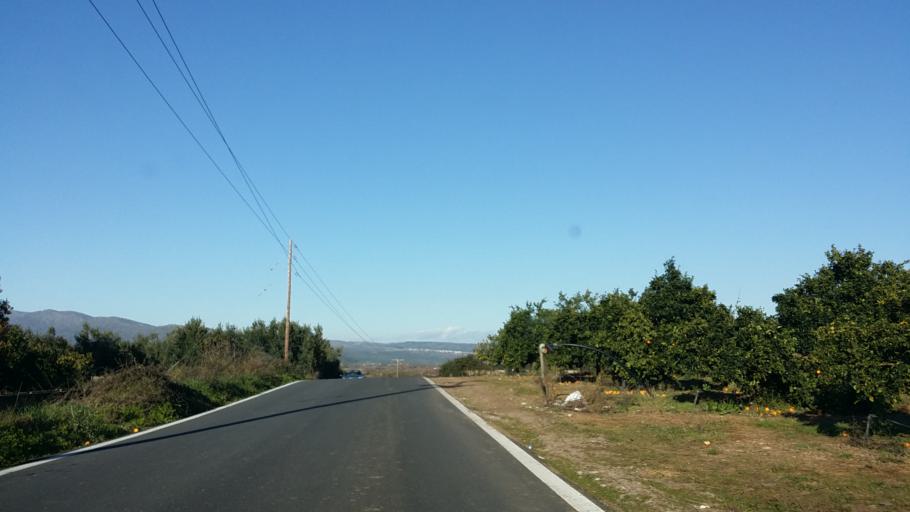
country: GR
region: West Greece
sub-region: Nomos Aitolias kai Akarnanias
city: Angelokastro
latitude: 38.6319
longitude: 21.2420
